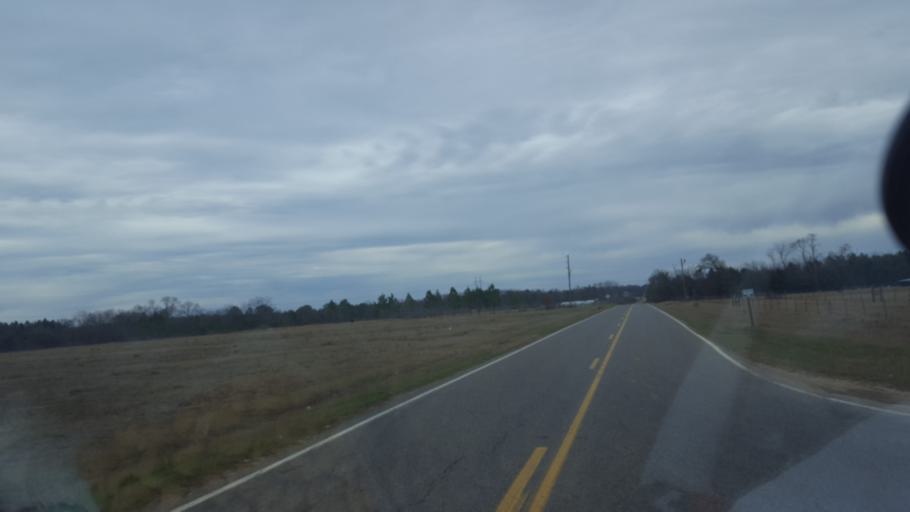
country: US
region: Georgia
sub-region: Ben Hill County
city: Fitzgerald
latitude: 31.7438
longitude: -83.3098
